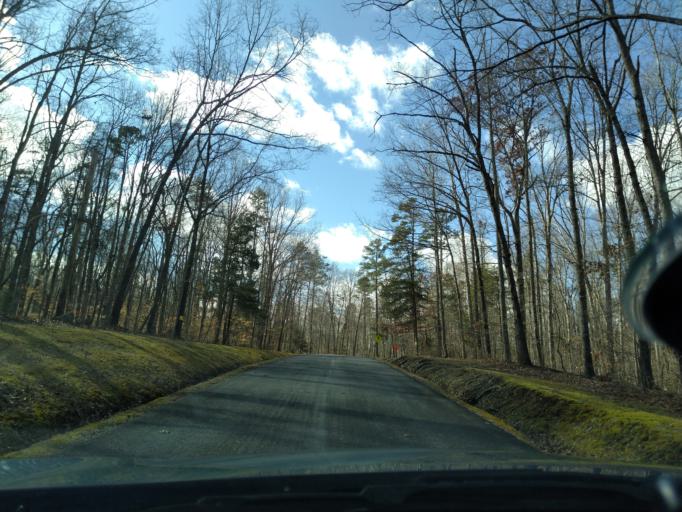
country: US
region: Virginia
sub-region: Nottoway County
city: Crewe
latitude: 37.1762
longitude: -78.2763
